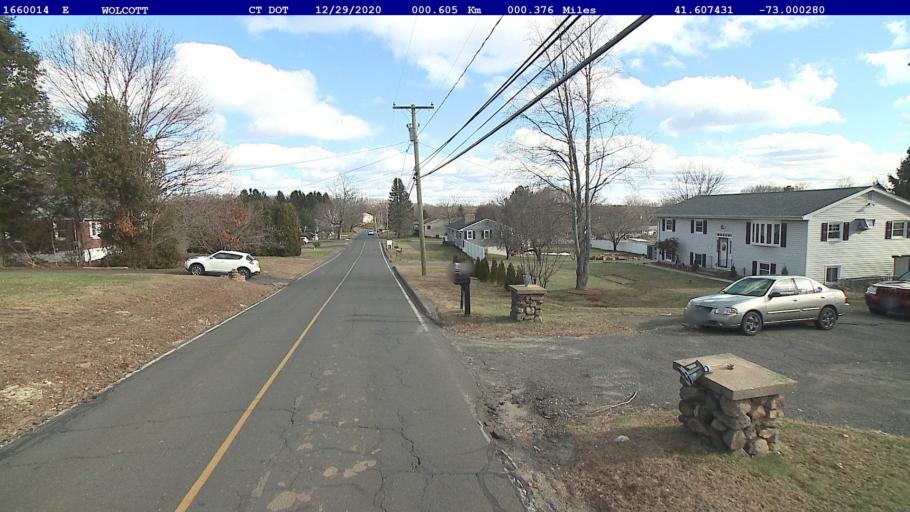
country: US
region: Connecticut
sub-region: New Haven County
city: Wolcott
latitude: 41.6074
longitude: -73.0003
